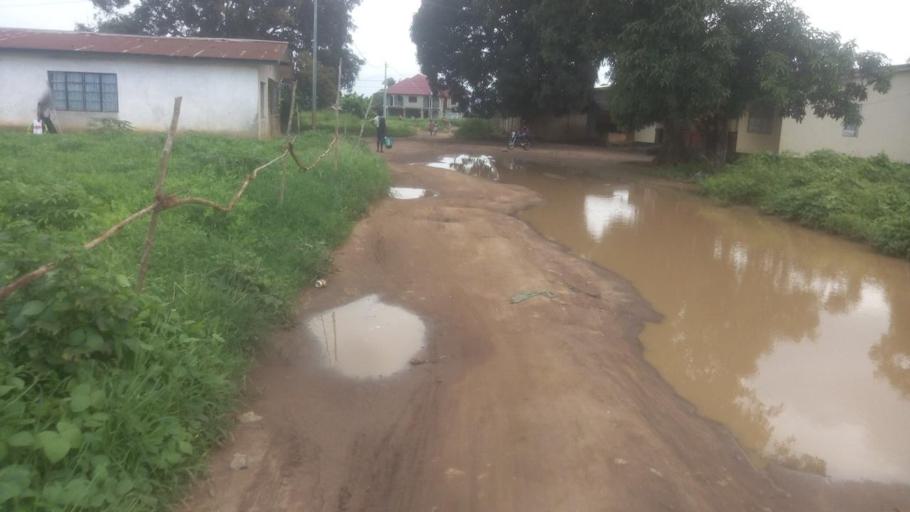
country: SL
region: Northern Province
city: Masoyila
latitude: 8.6029
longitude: -13.1851
